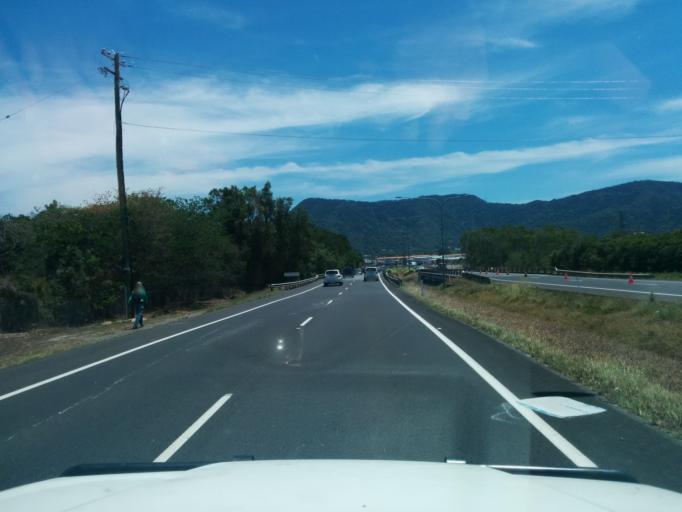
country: AU
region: Queensland
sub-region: Cairns
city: Woree
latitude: -16.9489
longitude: 145.7564
